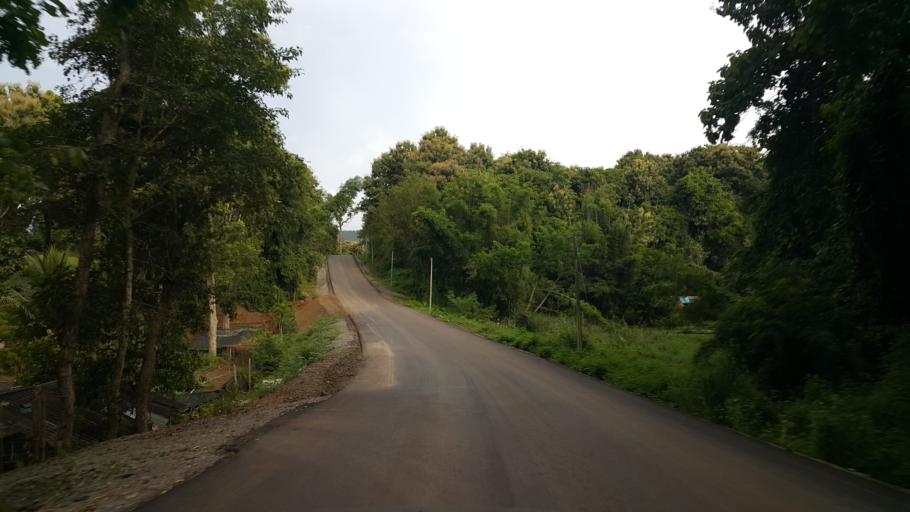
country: TH
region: Chiang Mai
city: Mae On
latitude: 18.8968
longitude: 99.2236
